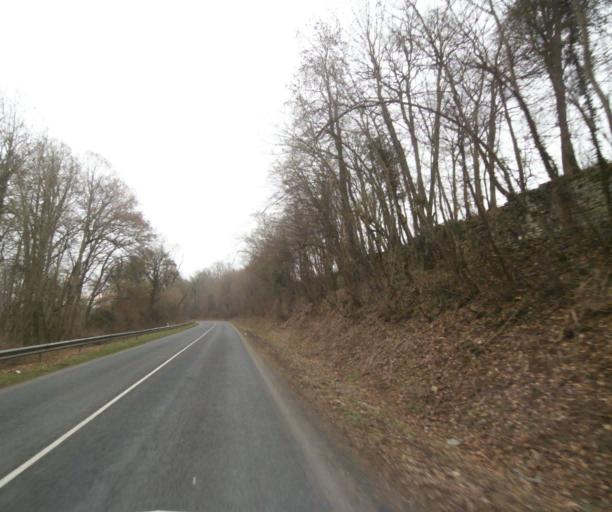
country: FR
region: Champagne-Ardenne
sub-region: Departement de la Haute-Marne
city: Bienville
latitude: 48.5595
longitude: 5.0571
